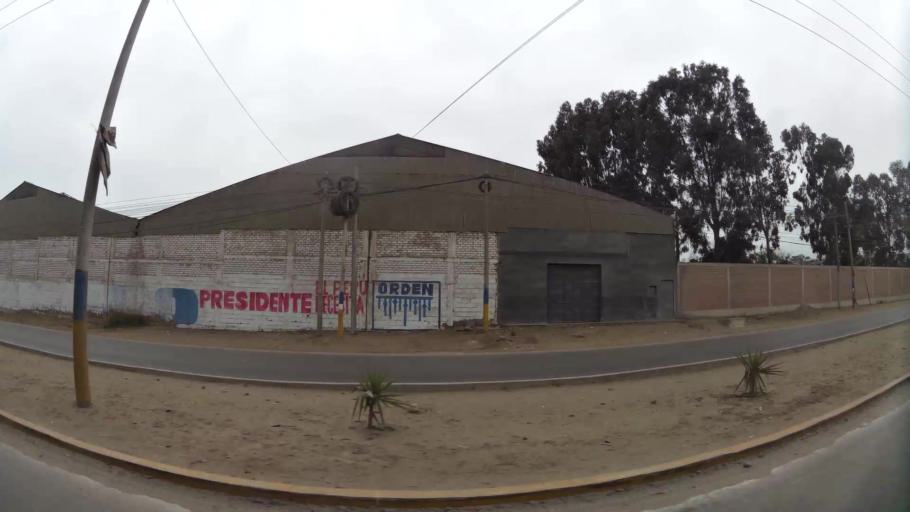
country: PE
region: Lima
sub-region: Lima
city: Surco
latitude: -12.2112
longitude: -76.9621
